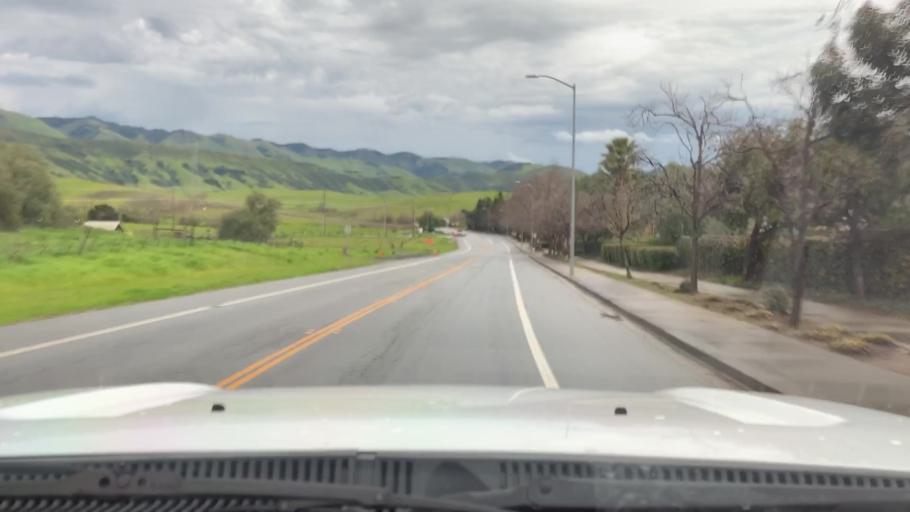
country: US
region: California
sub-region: San Luis Obispo County
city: San Luis Obispo
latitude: 35.2503
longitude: -120.6282
